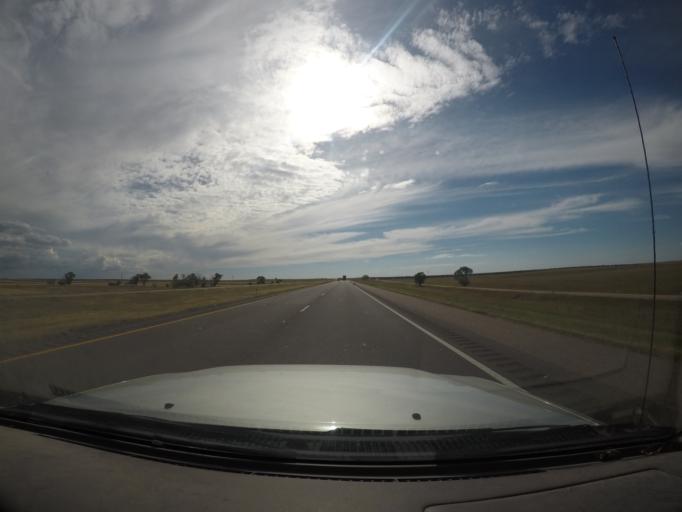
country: US
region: Nebraska
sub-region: Kimball County
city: Kimball
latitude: 41.1921
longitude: -103.8211
